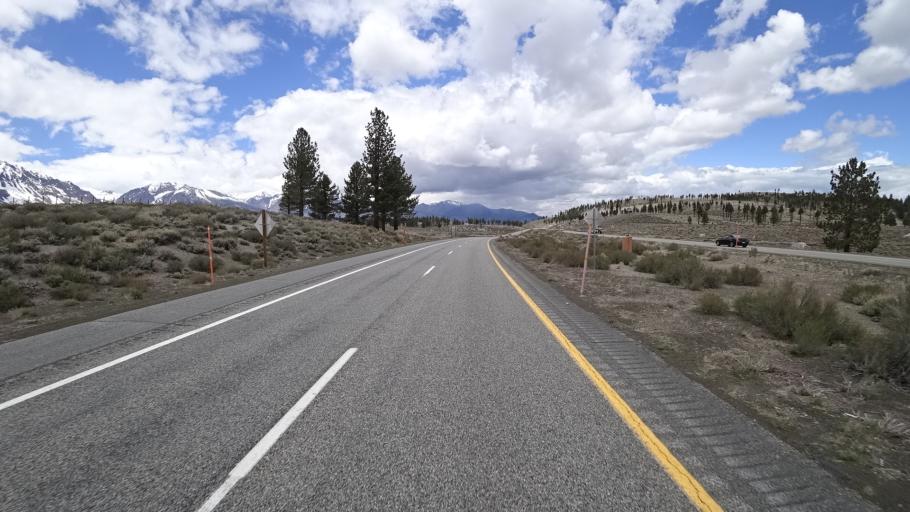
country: US
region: California
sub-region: Mono County
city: Mammoth Lakes
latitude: 37.8179
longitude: -119.0599
